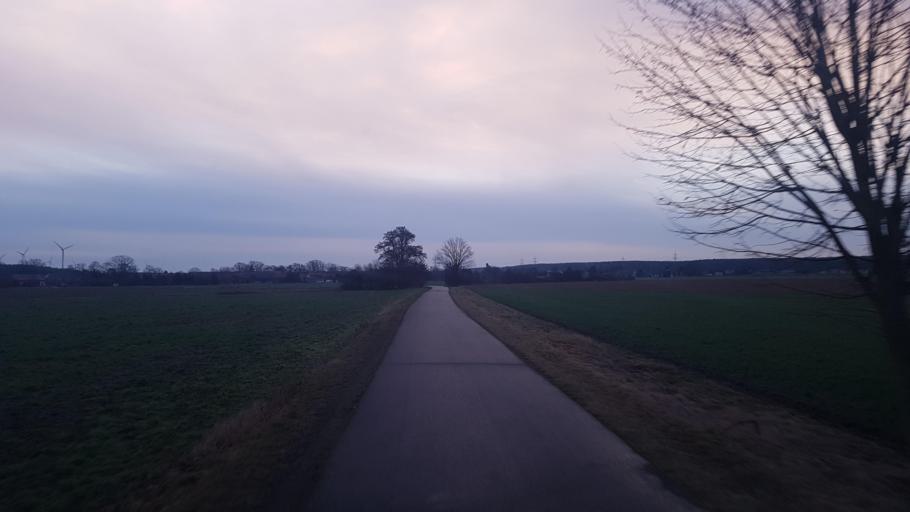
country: DE
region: Brandenburg
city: Dahme
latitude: 51.8684
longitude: 13.4520
